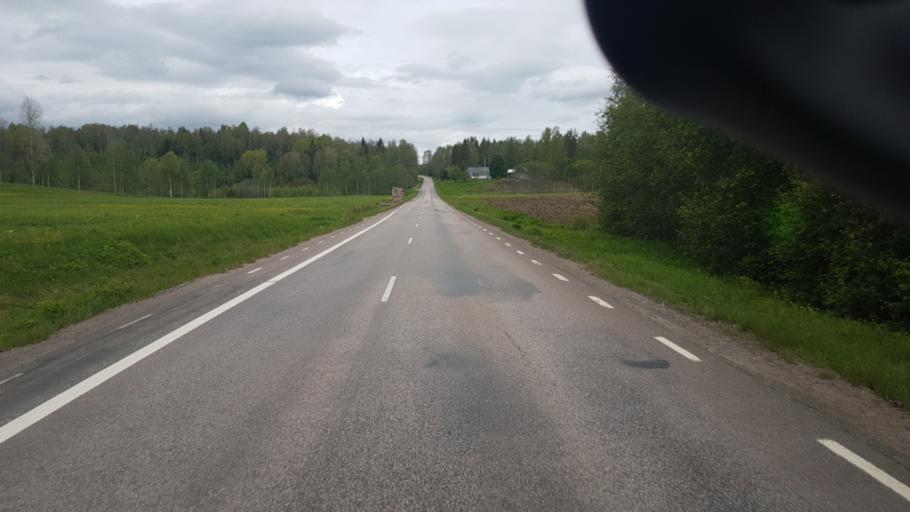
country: SE
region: Vaermland
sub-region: Arvika Kommun
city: Arvika
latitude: 59.8092
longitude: 12.5937
